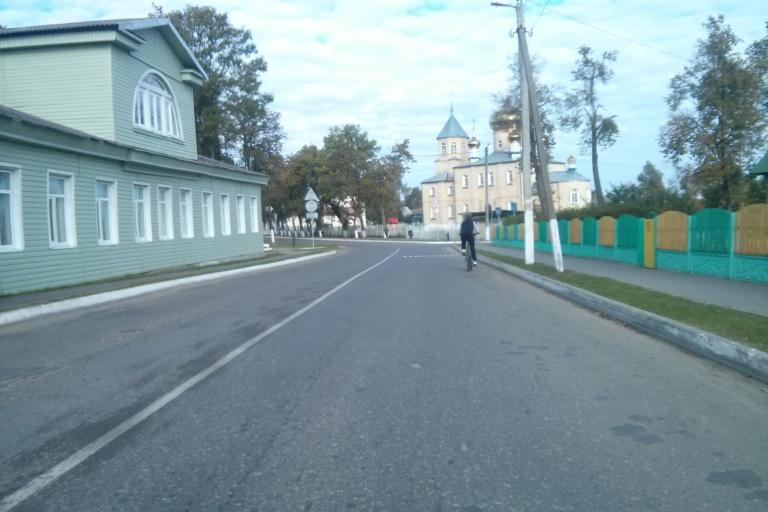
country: BY
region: Minsk
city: Chervyen'
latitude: 53.7114
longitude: 28.4250
